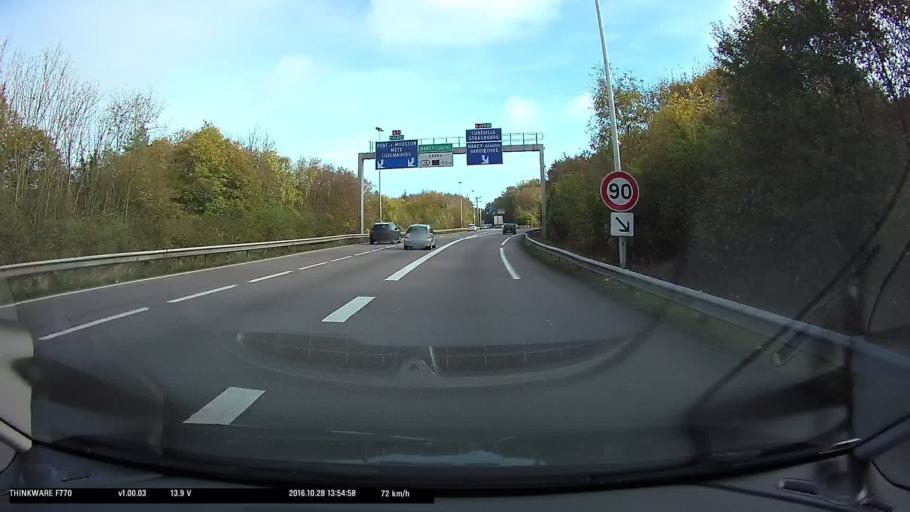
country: FR
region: Lorraine
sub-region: Departement de Meurthe-et-Moselle
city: Laxou
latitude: 48.6945
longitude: 6.1108
